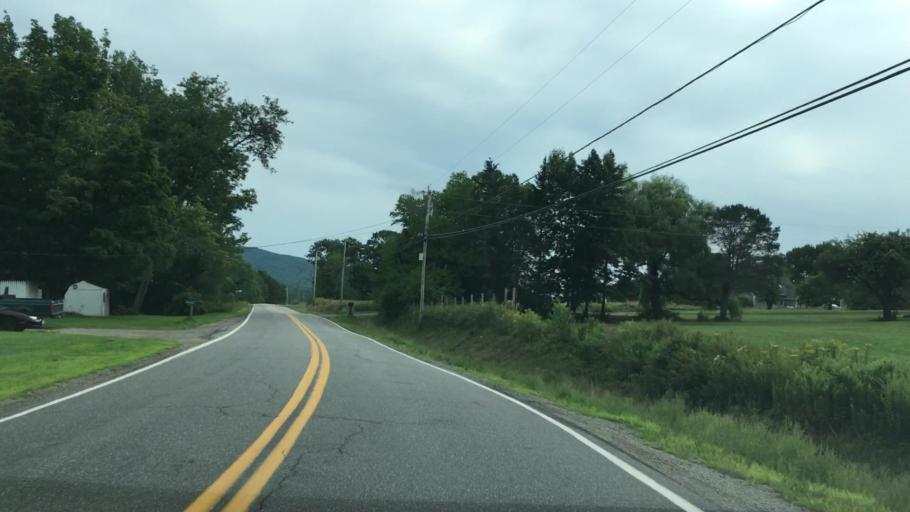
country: US
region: Maine
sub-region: Waldo County
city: Lincolnville
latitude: 44.3124
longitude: -69.0877
